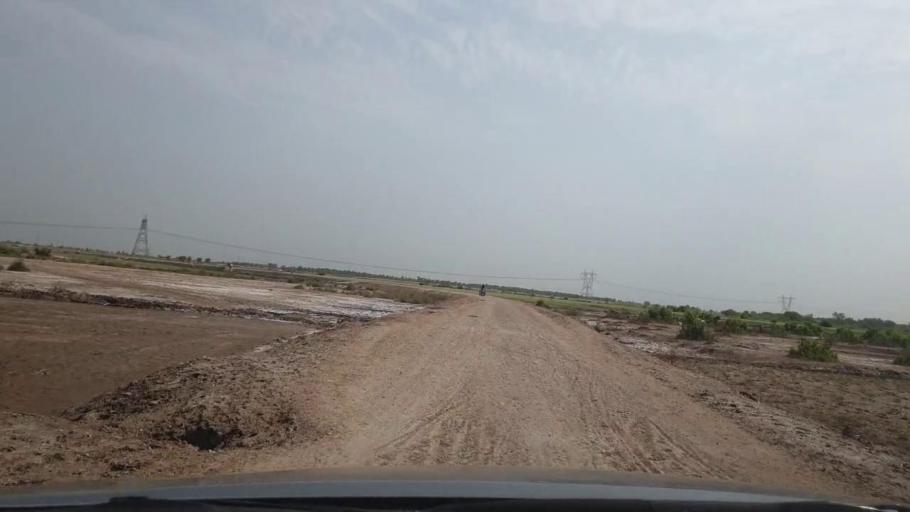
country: PK
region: Sindh
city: Rohri
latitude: 27.6692
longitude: 69.0261
